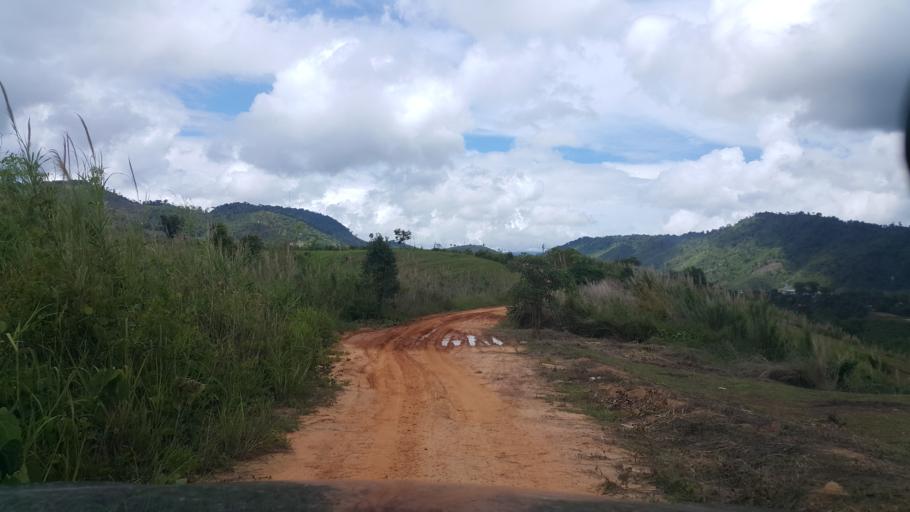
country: TH
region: Loei
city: Na Haeo
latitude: 17.5927
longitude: 100.8973
